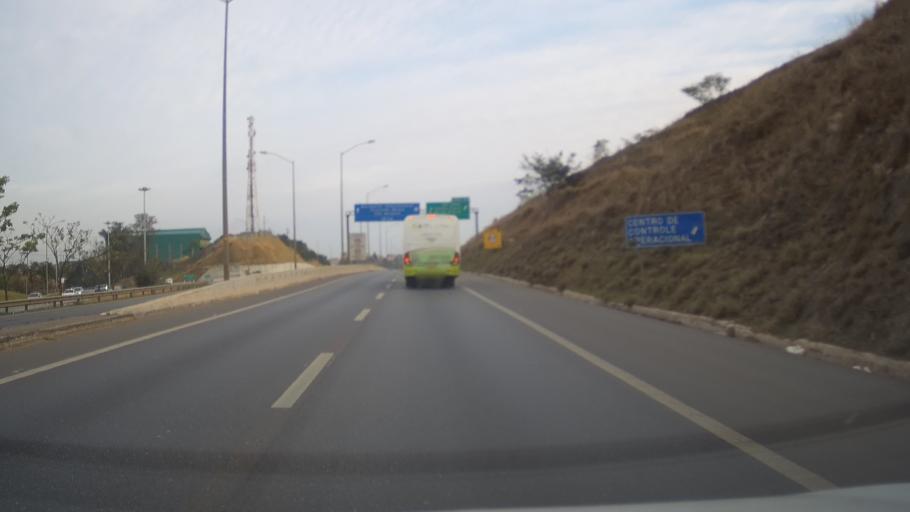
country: BR
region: Minas Gerais
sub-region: Vespasiano
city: Vespasiano
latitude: -19.7619
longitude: -43.9479
